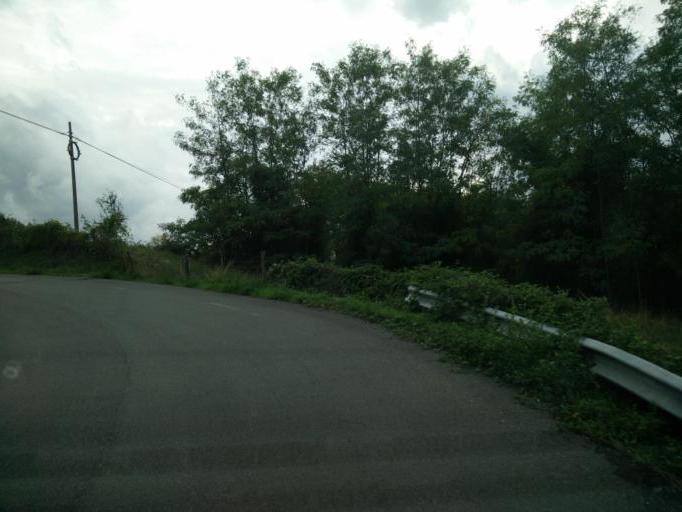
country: IT
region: Tuscany
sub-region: Provincia di Massa-Carrara
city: Casola in Lunigiana
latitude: 44.2157
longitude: 10.1976
